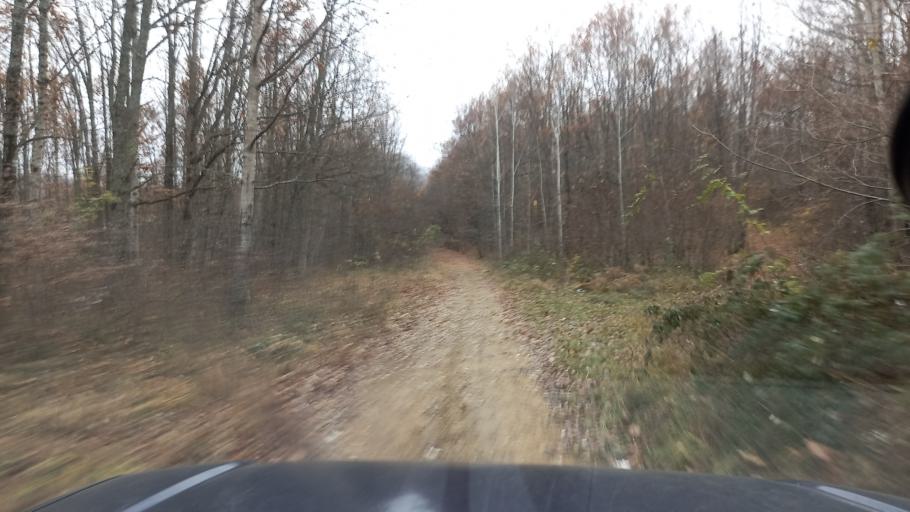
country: RU
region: Krasnodarskiy
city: Goryachiy Klyuch
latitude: 44.4982
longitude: 39.2790
